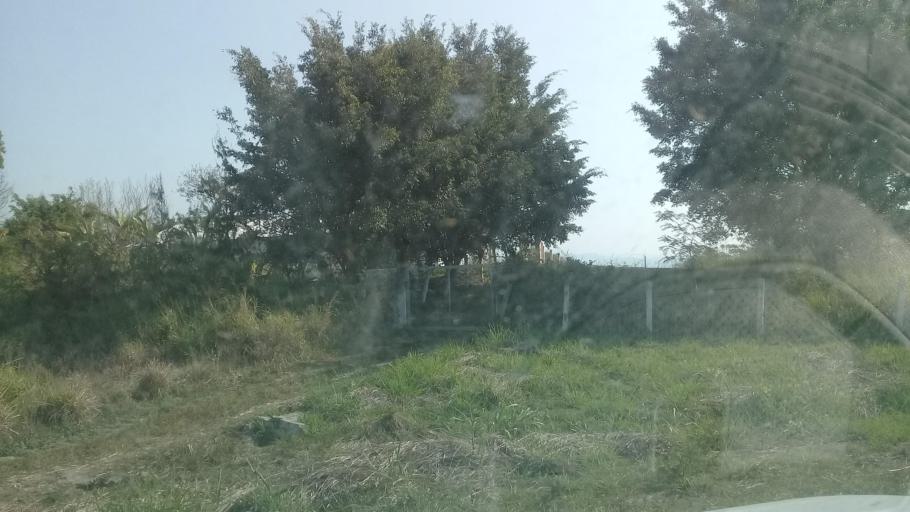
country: MX
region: Veracruz
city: El Castillo
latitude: 19.5748
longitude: -96.8369
